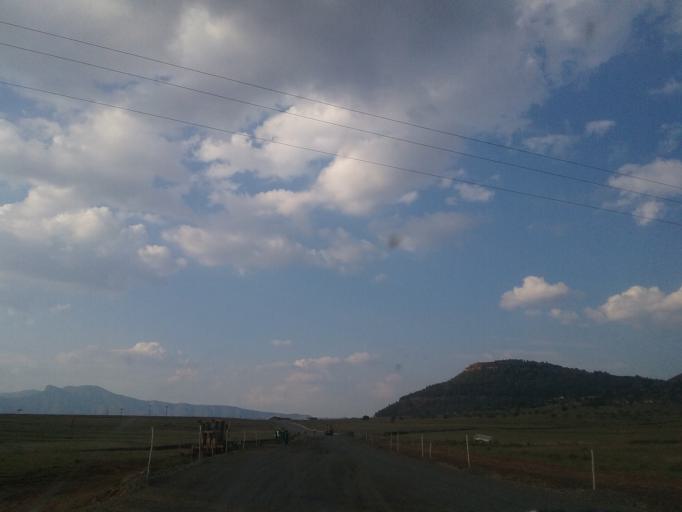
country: LS
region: Quthing
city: Quthing
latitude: -30.4073
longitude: 27.6062
